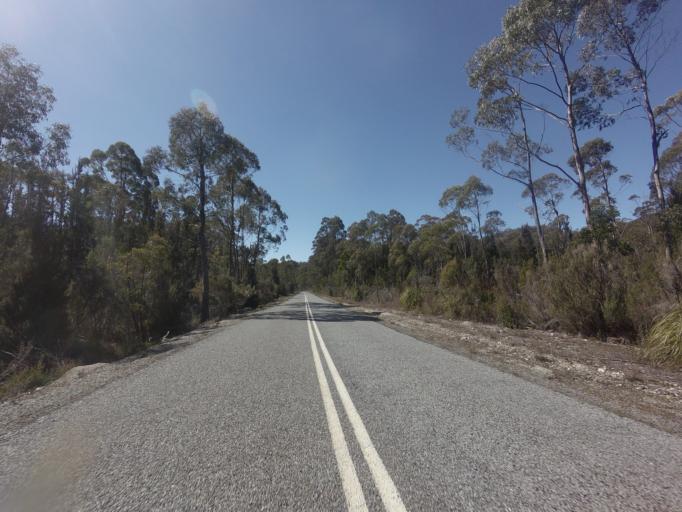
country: AU
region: Tasmania
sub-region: Huon Valley
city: Geeveston
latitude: -42.7697
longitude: 146.3968
